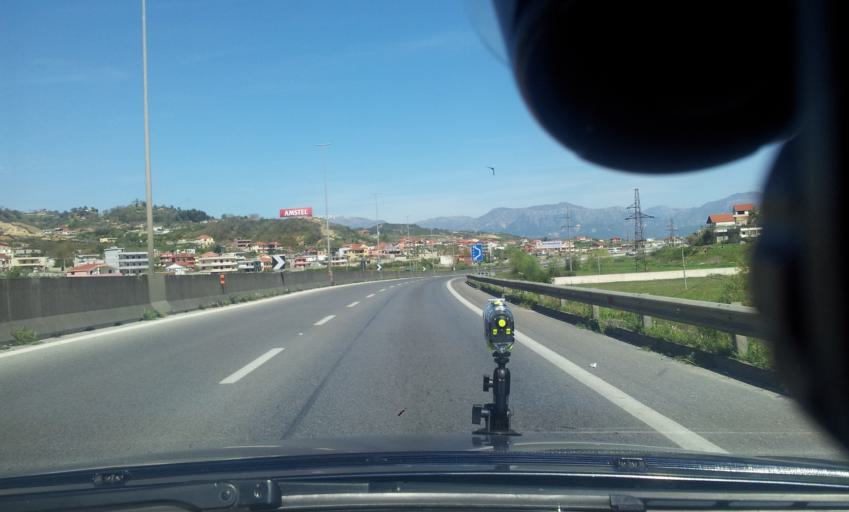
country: AL
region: Tirane
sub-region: Rrethi i Tiranes
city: Vore
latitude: 41.3988
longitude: 19.6398
